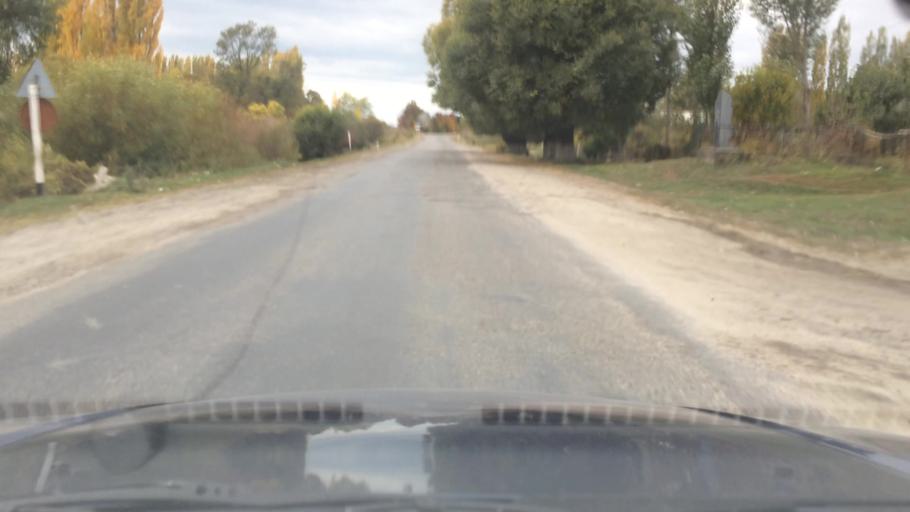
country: KG
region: Ysyk-Koel
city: Tyup
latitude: 42.7675
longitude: 78.1840
